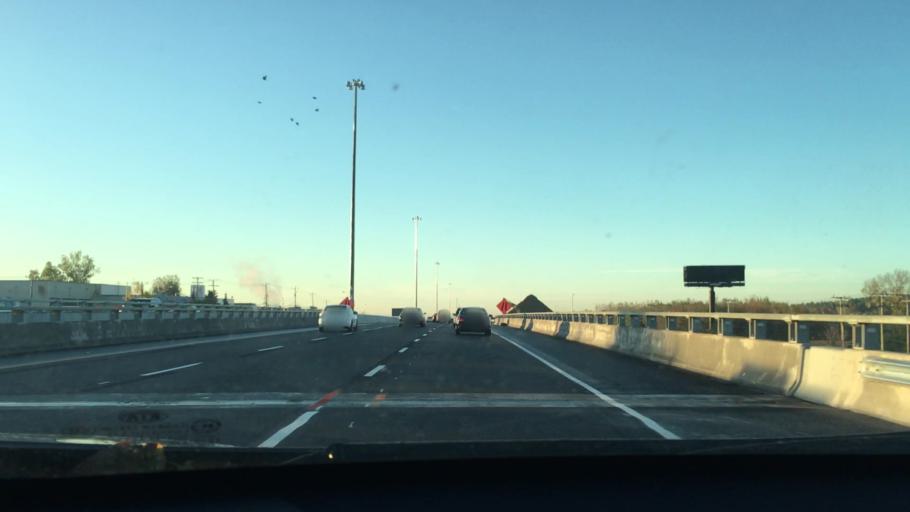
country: CA
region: Quebec
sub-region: Laurentides
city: Saint-Jerome
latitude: 45.7878
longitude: -74.0206
